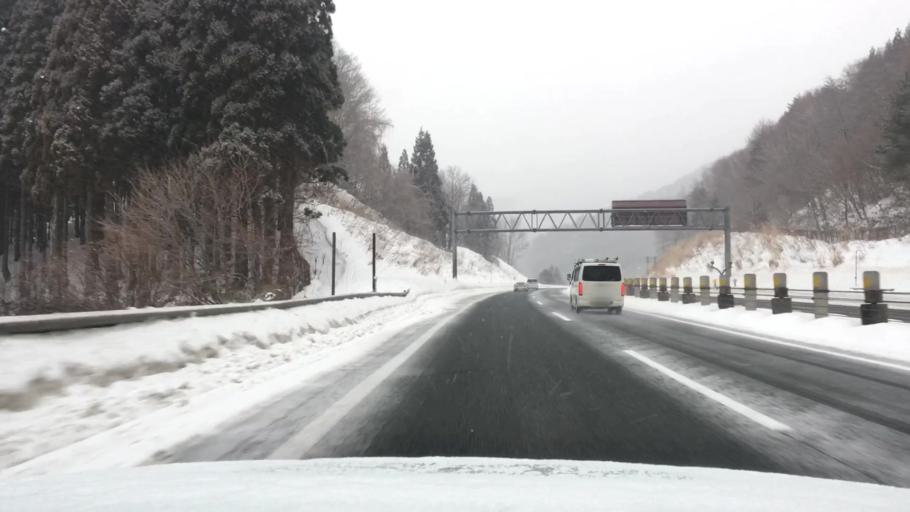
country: JP
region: Akita
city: Hanawa
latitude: 40.1118
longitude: 141.0358
